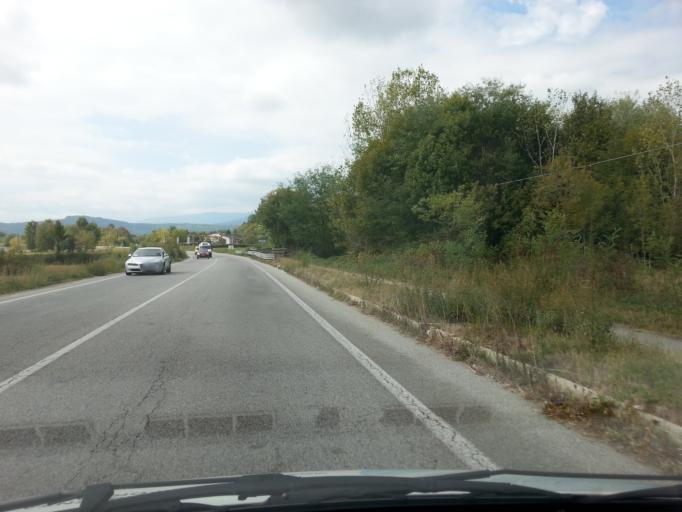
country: IT
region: Piedmont
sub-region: Provincia di Torino
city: Frossasco
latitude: 44.9419
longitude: 7.3766
